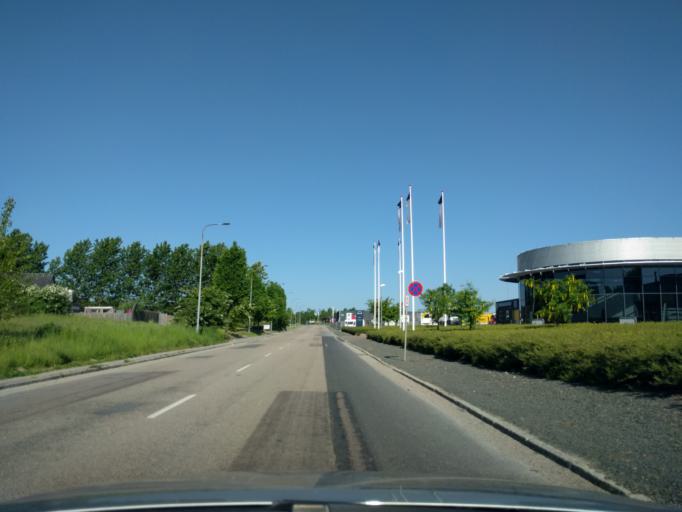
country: DK
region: South Denmark
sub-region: Odense Kommune
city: Bellinge
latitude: 55.3553
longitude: 10.3331
